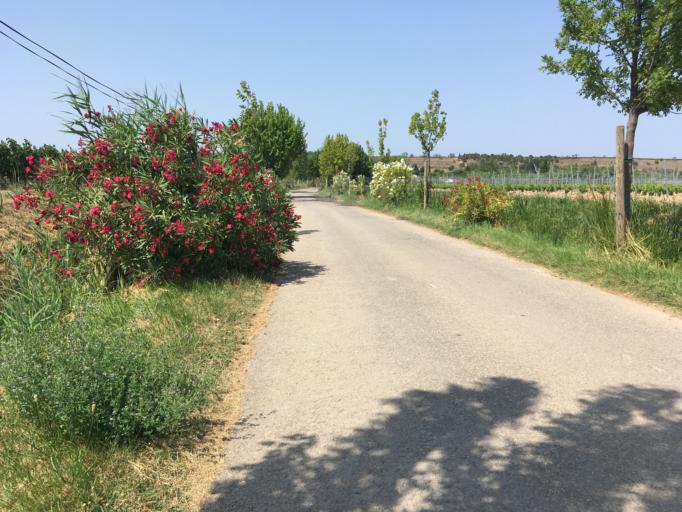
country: FR
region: Languedoc-Roussillon
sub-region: Departement de l'Aude
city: Puicheric
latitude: 43.2277
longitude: 2.6224
